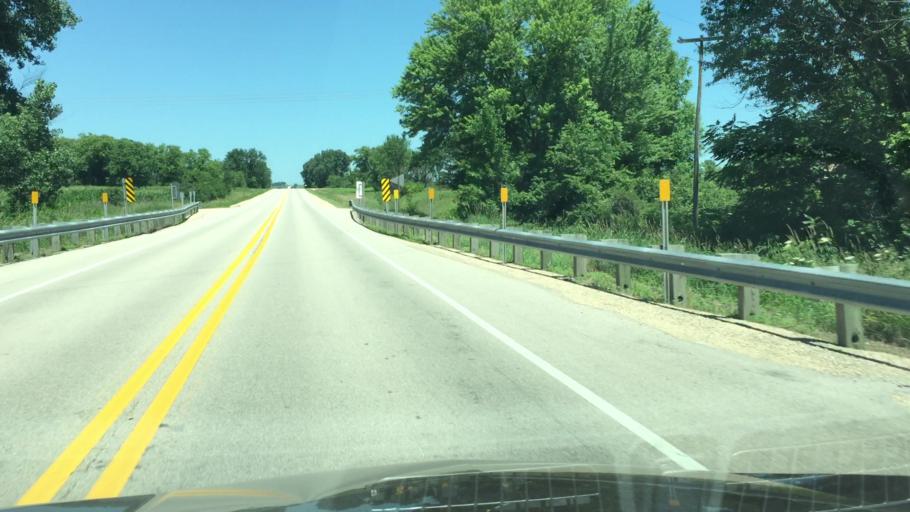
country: US
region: Iowa
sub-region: Jones County
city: Anamosa
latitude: 42.0272
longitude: -91.1367
